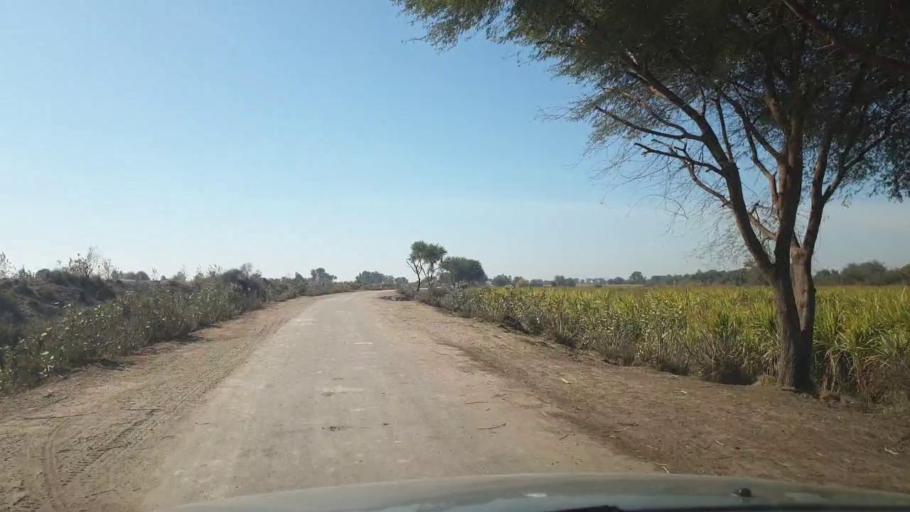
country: PK
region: Sindh
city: Ghotki
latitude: 28.0172
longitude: 69.2668
